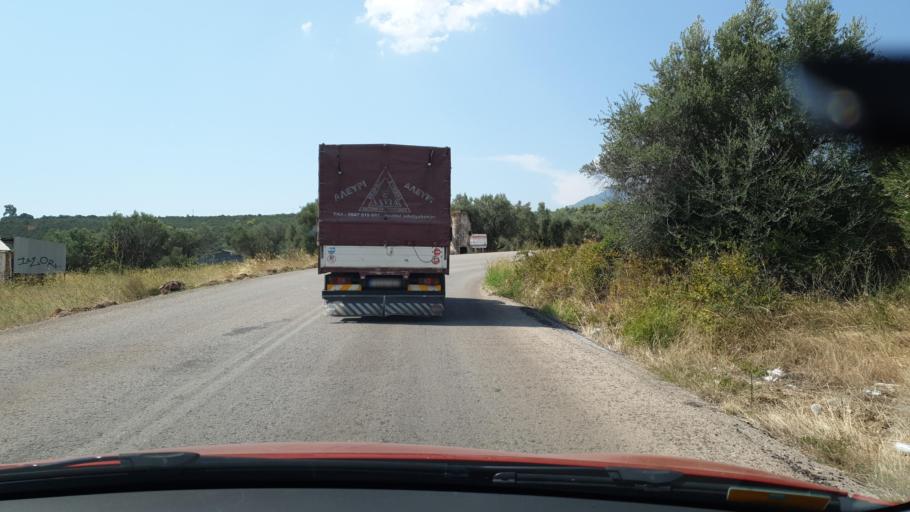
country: GR
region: Central Greece
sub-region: Nomos Evvoias
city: Psachna
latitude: 38.5819
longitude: 23.6107
